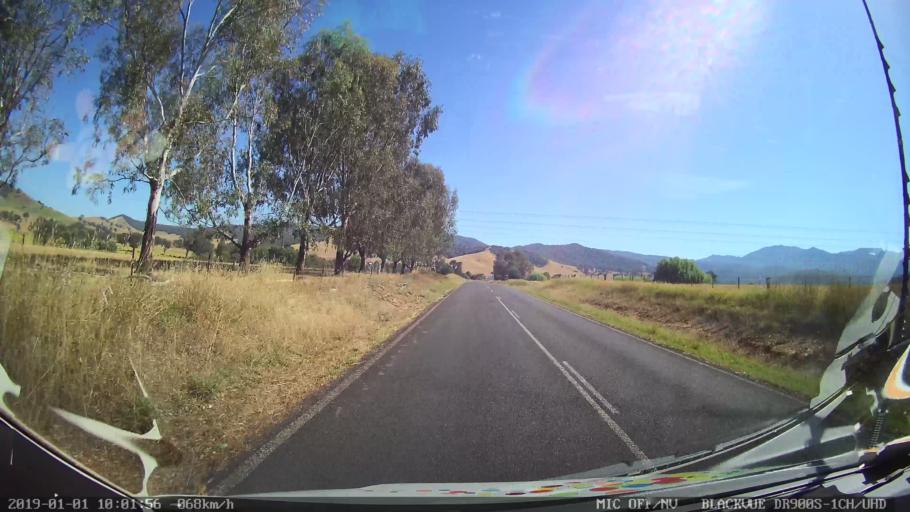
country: AU
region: New South Wales
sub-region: Snowy River
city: Jindabyne
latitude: -36.1863
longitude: 148.1011
